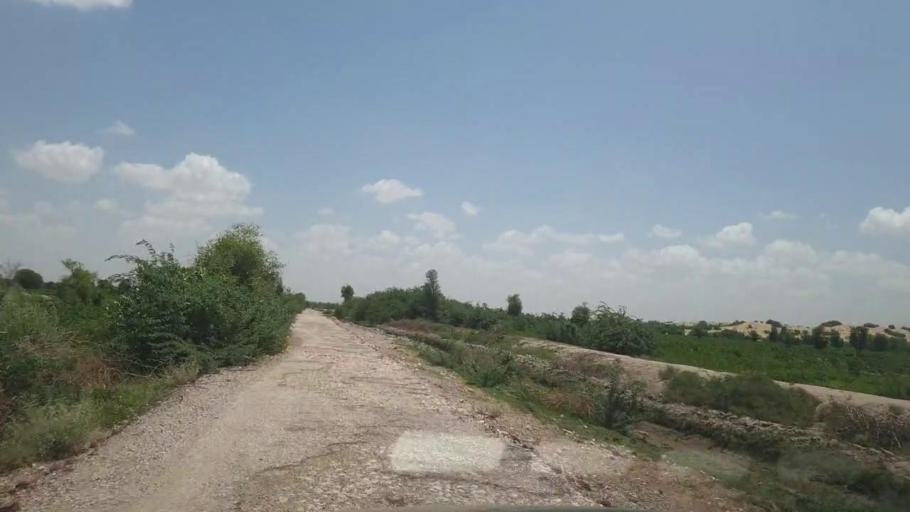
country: PK
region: Sindh
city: Kot Diji
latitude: 27.2917
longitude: 69.0854
